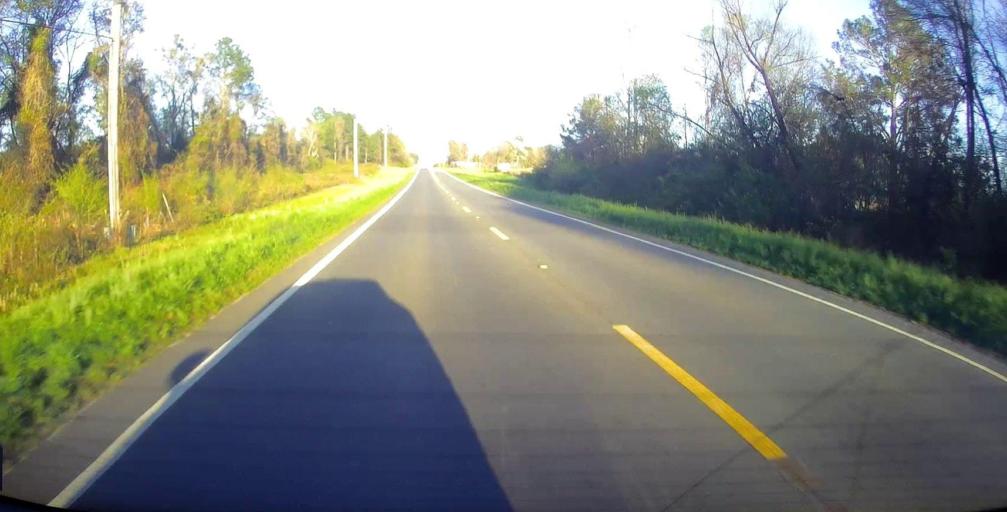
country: US
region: Georgia
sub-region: Wilcox County
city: Rochelle
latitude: 31.9505
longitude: -83.4694
